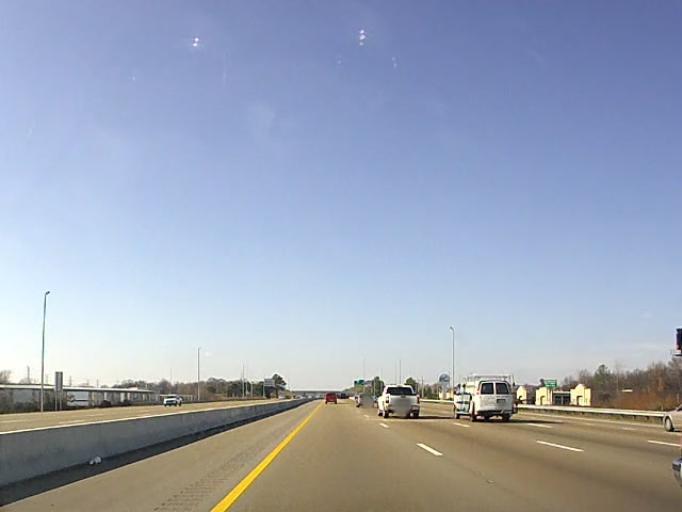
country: US
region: Tennessee
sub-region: Shelby County
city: Germantown
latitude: 35.0793
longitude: -89.9256
